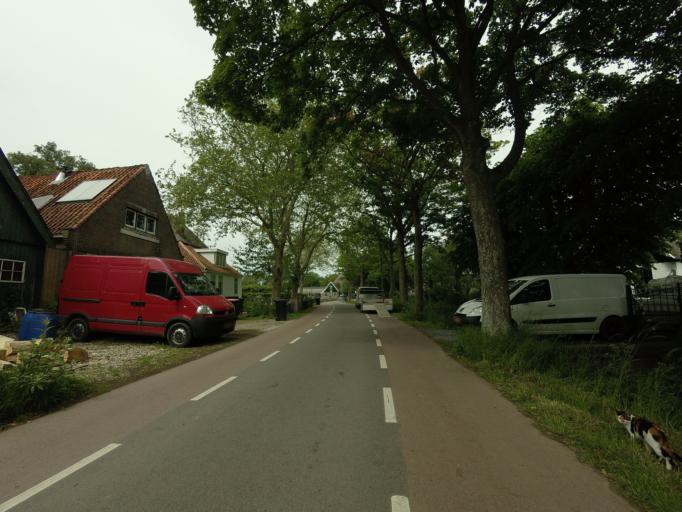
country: NL
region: North Holland
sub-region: Gemeente Hoorn
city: Hoorn
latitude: 52.6376
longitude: 5.1227
